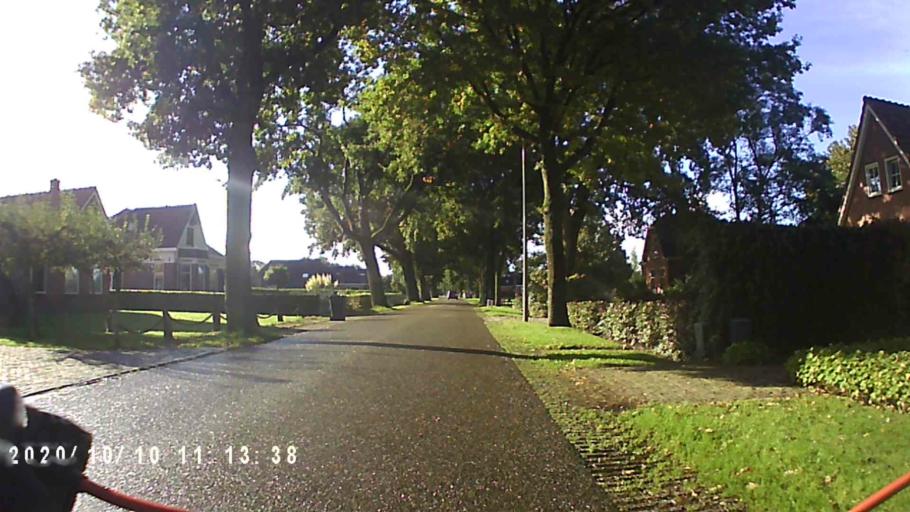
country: NL
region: Friesland
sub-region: Gemeente Smallingerland
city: Drachtstercompagnie
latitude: 53.1082
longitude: 6.2044
